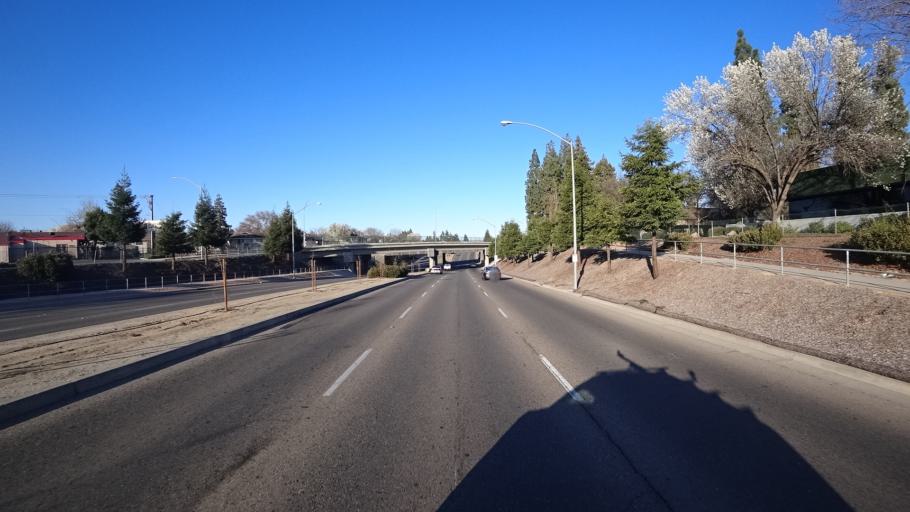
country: US
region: California
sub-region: Fresno County
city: Fresno
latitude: 36.8083
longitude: -119.8396
